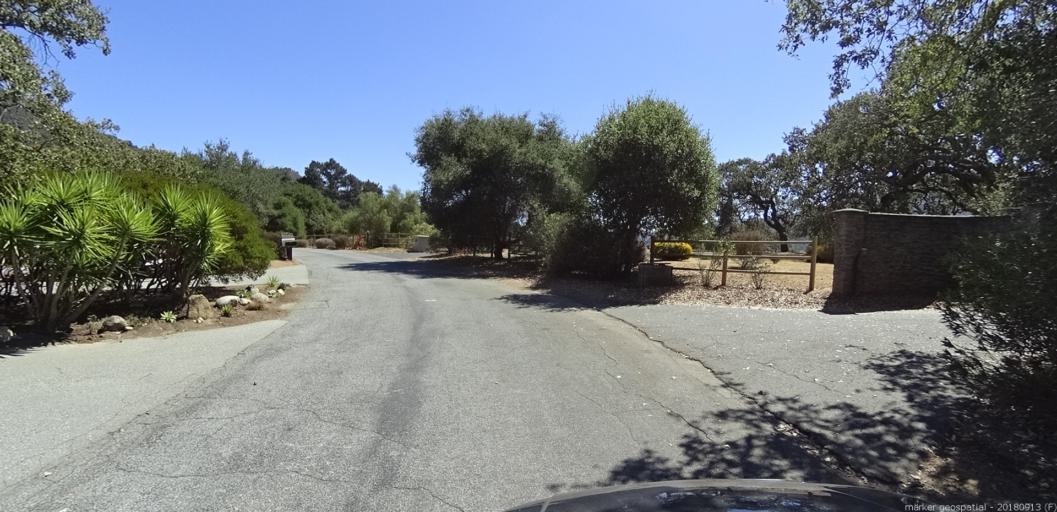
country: US
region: California
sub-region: Monterey County
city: Carmel Valley Village
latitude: 36.5038
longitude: -121.7534
